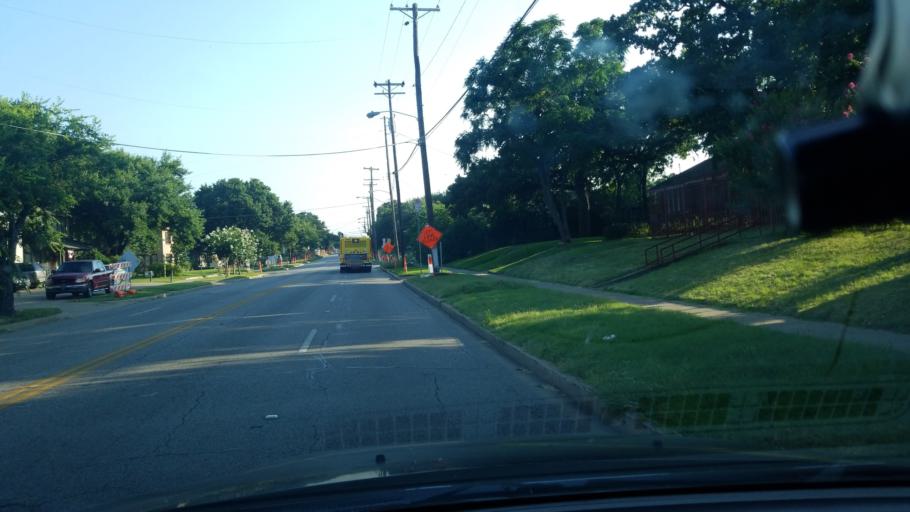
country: US
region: Texas
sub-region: Dallas County
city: Dallas
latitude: 32.7540
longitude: -96.8156
